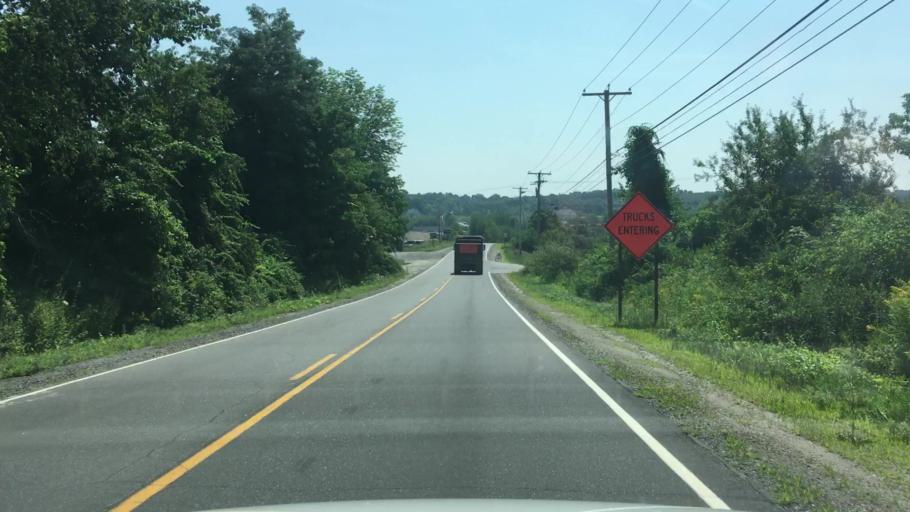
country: US
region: Maine
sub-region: Kennebec County
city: Hallowell
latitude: 44.3017
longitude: -69.8157
